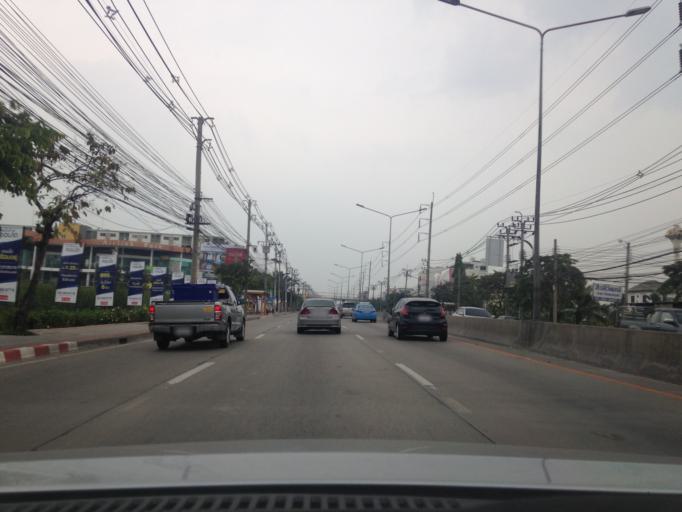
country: TH
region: Bangkok
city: Lat Krabang
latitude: 13.7353
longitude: 100.7464
